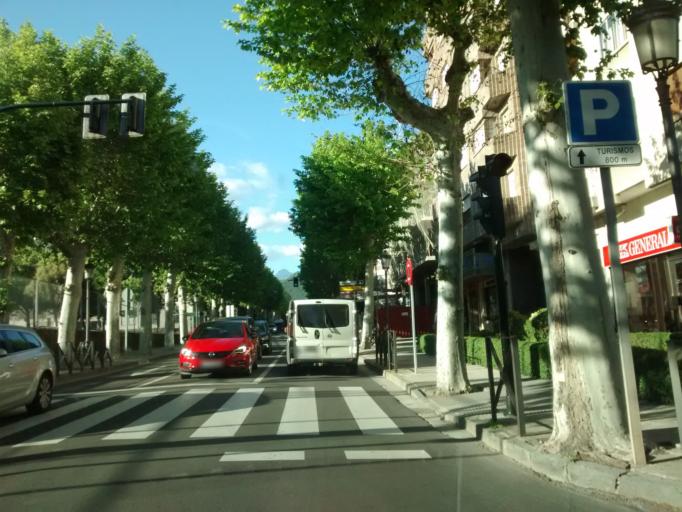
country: ES
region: Aragon
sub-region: Provincia de Huesca
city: Jaca
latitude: 42.5679
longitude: -0.5530
